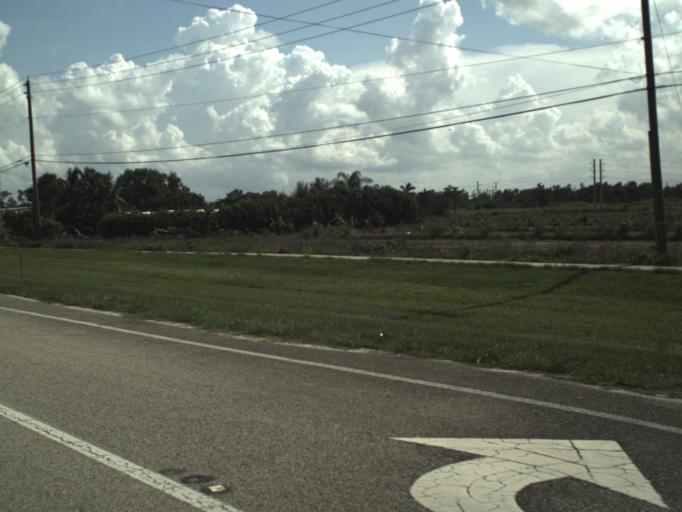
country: US
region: Florida
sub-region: Palm Beach County
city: Villages of Oriole
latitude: 26.4969
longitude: -80.2052
